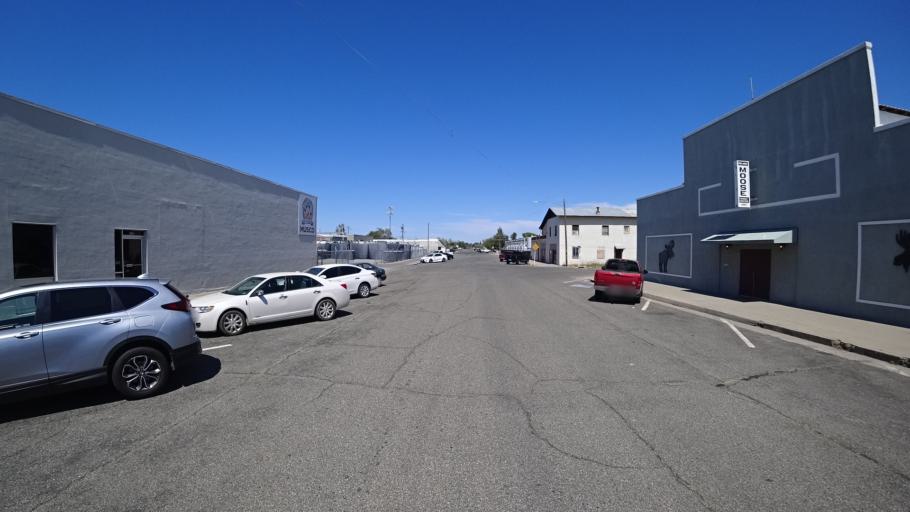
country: US
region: California
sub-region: Glenn County
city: Orland
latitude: 39.7482
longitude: -122.1955
